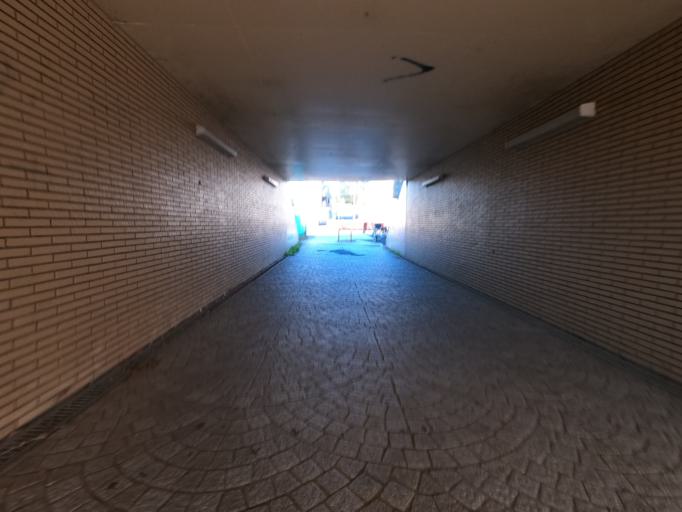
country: JP
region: Ibaraki
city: Moriya
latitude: 35.9344
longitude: 140.0020
